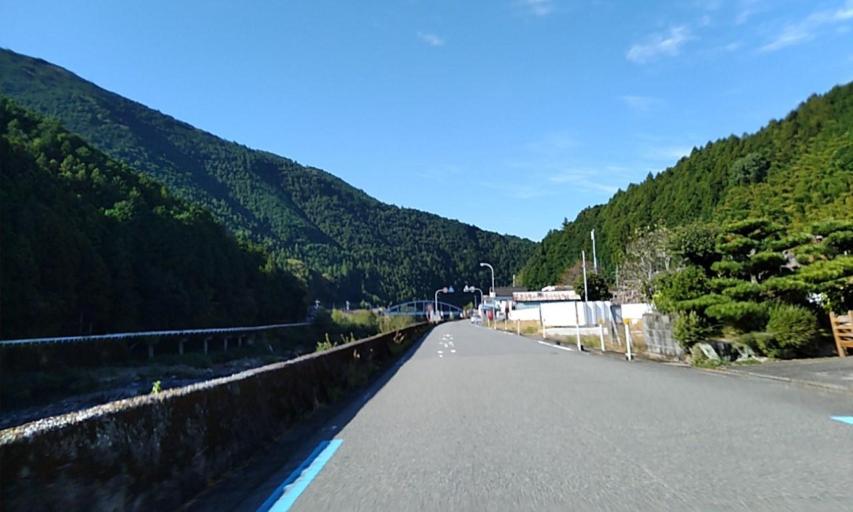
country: JP
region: Wakayama
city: Kainan
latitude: 34.0480
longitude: 135.3449
